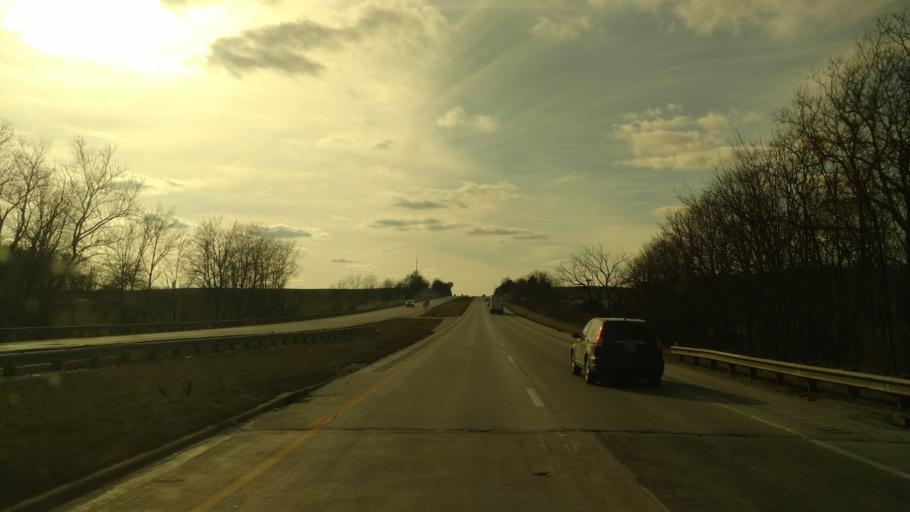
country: US
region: Ohio
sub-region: Medina County
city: Seville
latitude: 41.0330
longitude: -81.8517
